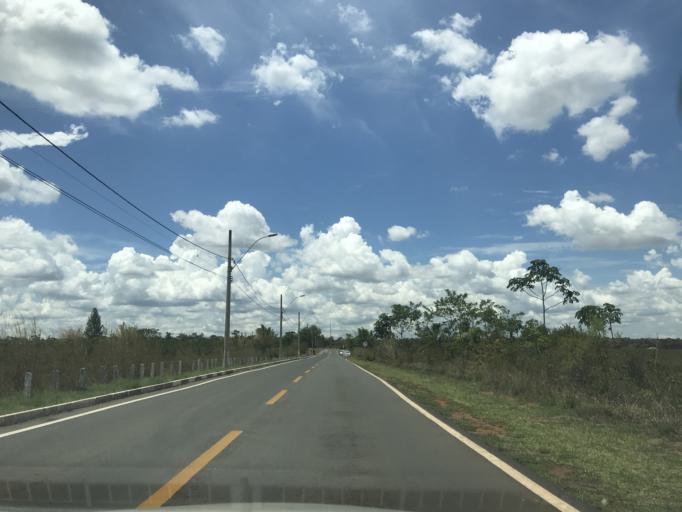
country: BR
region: Federal District
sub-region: Brasilia
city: Brasilia
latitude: -15.8985
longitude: -47.9440
